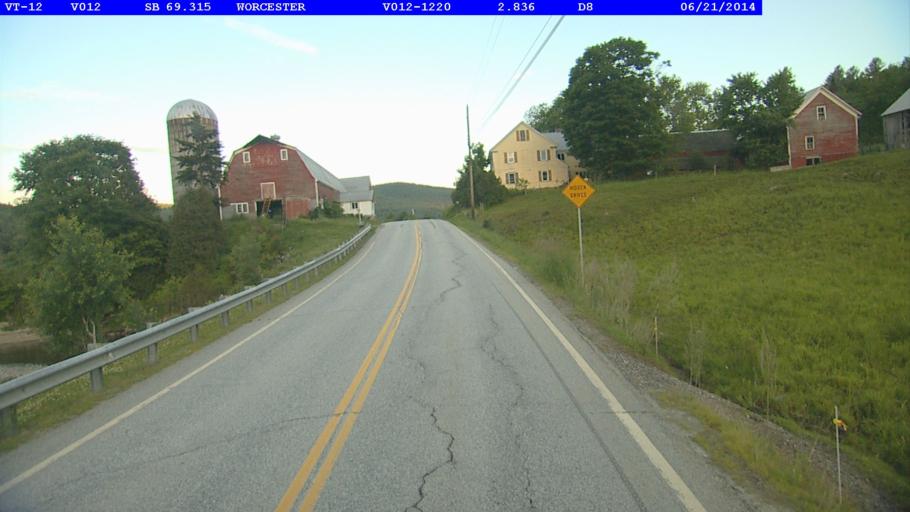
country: US
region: Vermont
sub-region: Washington County
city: Montpelier
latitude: 44.3883
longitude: -72.5560
